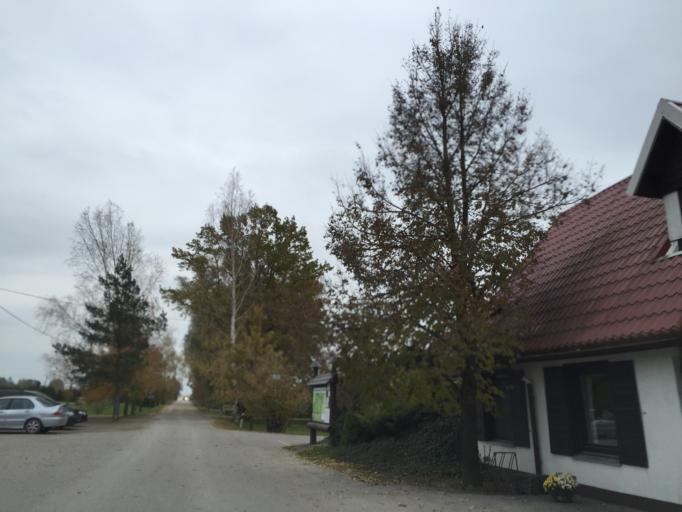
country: LV
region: Ozolnieku
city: Ozolnieki
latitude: 56.6402
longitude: 23.7776
